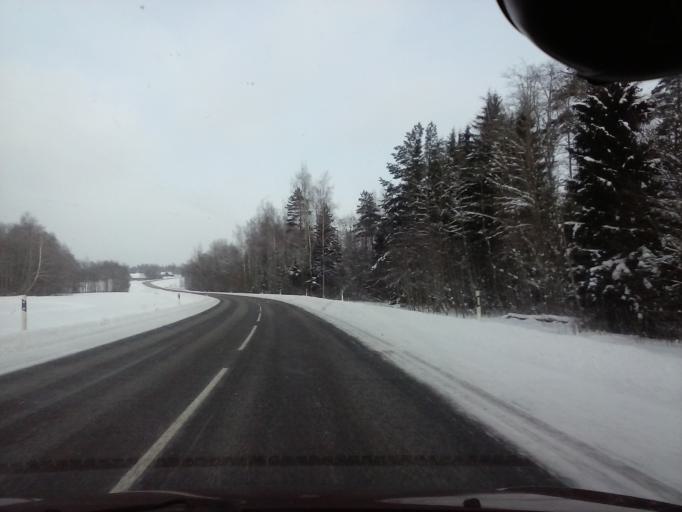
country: EE
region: Paernumaa
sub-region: Saarde vald
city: Kilingi-Nomme
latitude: 58.1703
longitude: 25.0283
